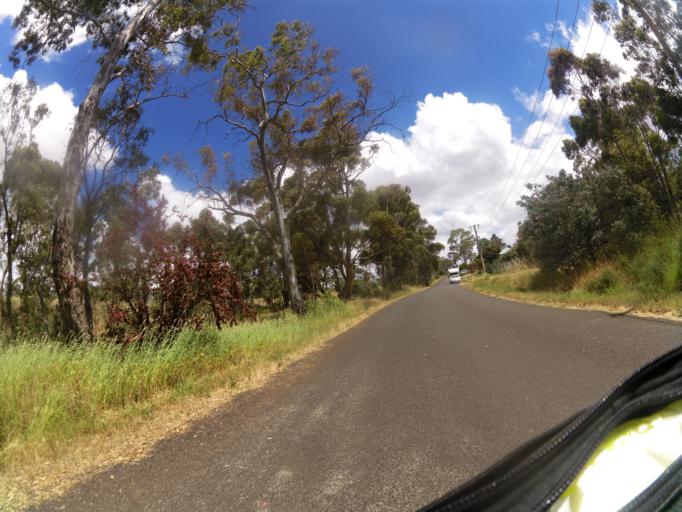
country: AU
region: Victoria
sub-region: Mount Alexander
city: Castlemaine
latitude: -37.0016
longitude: 144.2540
